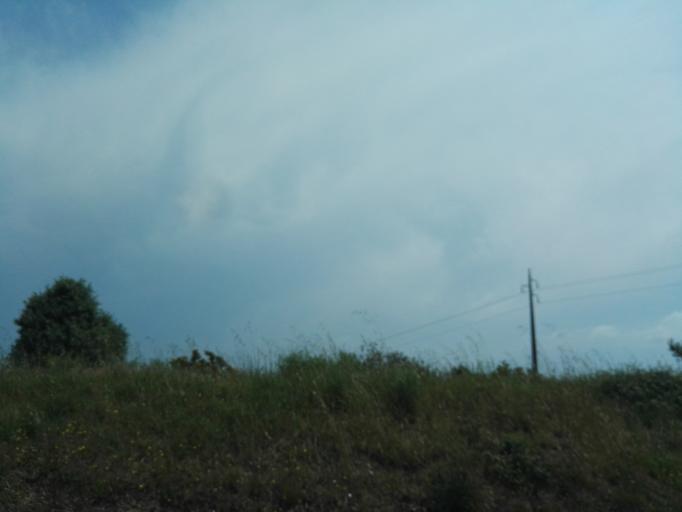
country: PT
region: Santarem
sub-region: Entroncamento
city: Entroncamento
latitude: 39.4750
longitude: -8.4590
